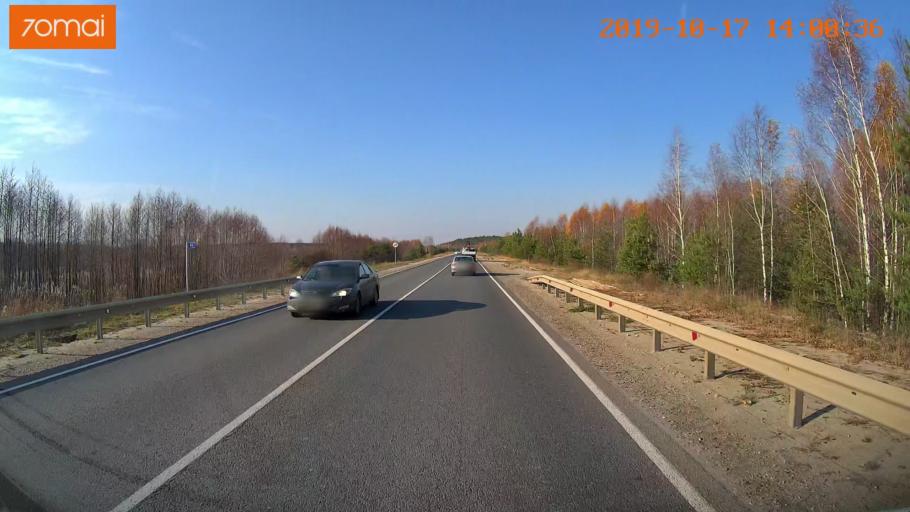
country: RU
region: Rjazan
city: Spas-Klepiki
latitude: 55.1470
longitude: 40.1774
